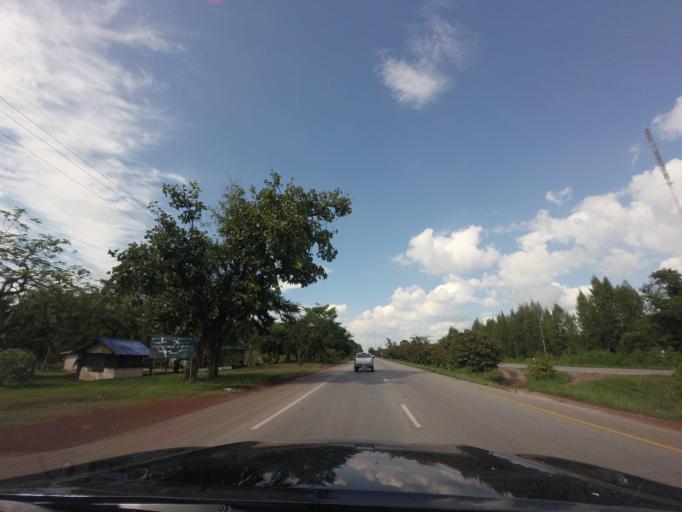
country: TH
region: Nong Khai
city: Sa Khrai
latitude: 17.6535
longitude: 102.7885
